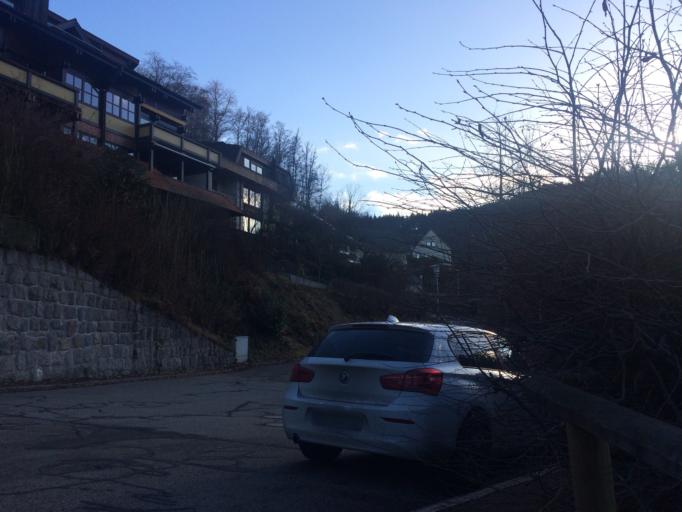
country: DE
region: Baden-Wuerttemberg
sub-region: Freiburg Region
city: Triberg im Schwarzwald
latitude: 48.1307
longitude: 8.2355
